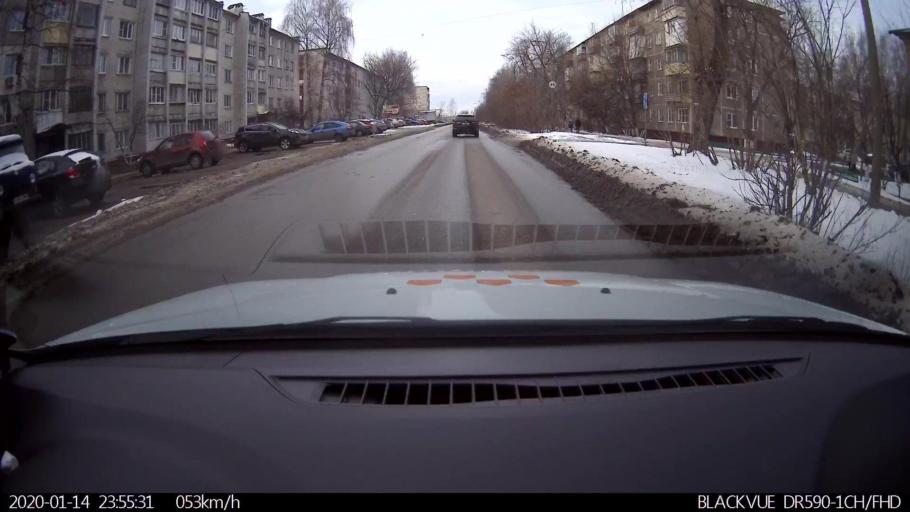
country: RU
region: Nizjnij Novgorod
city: Gorbatovka
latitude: 56.2662
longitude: 43.8705
